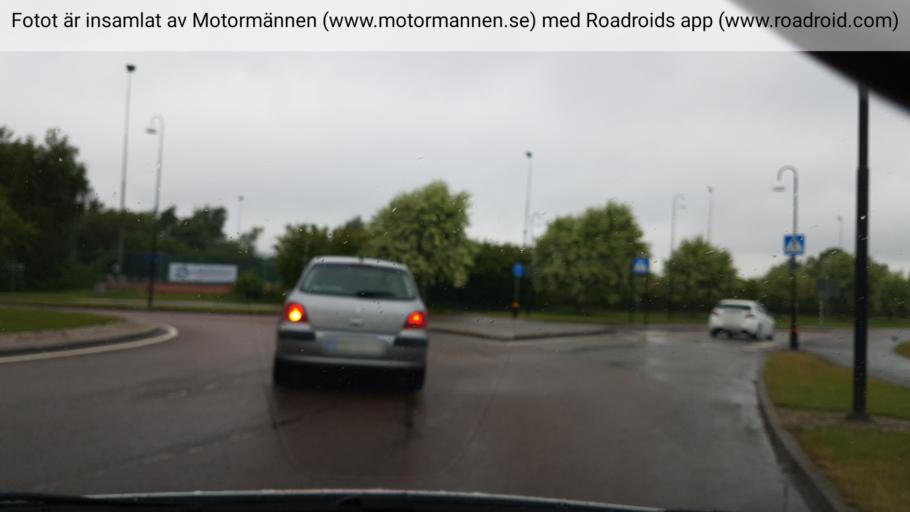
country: SE
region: Vaestra Goetaland
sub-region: Falkopings Kommun
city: Falkoeping
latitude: 58.1627
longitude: 13.5658
